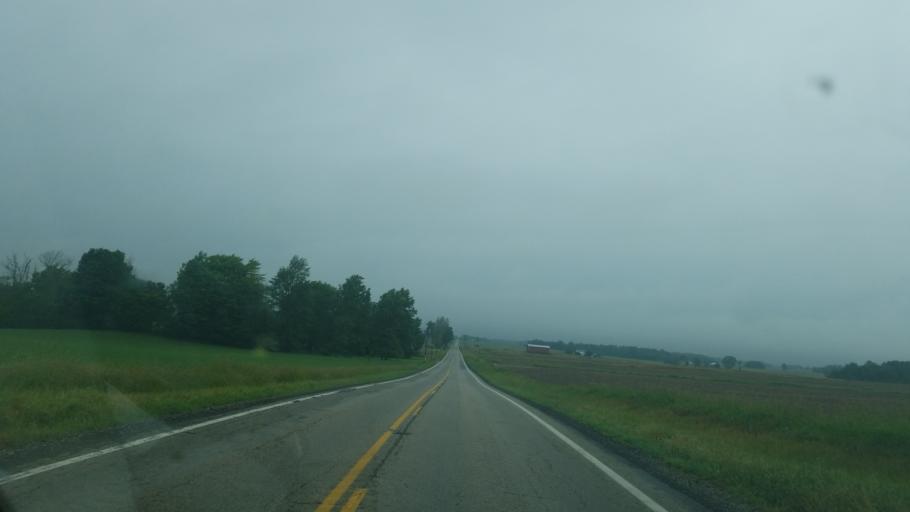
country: US
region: Ohio
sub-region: Crawford County
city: Bucyrus
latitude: 40.8768
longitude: -82.8549
